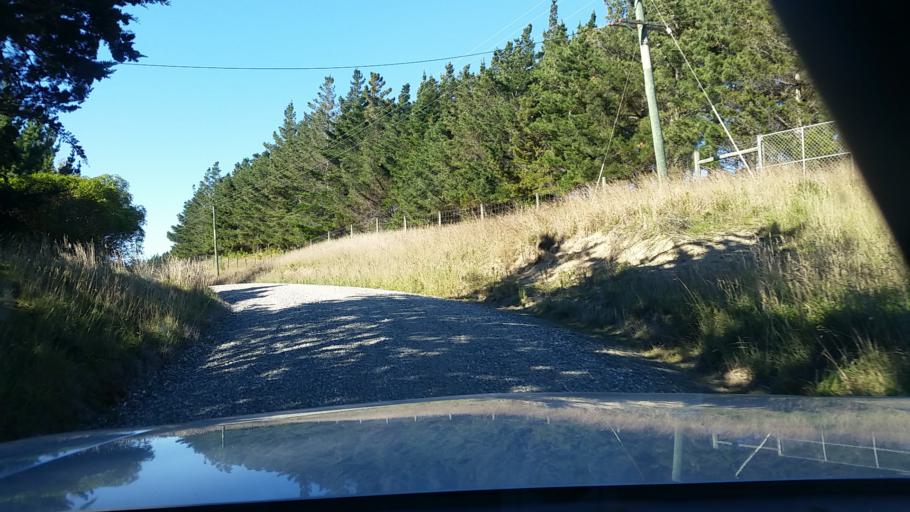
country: NZ
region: Marlborough
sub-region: Marlborough District
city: Blenheim
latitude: -41.6665
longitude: 174.1527
